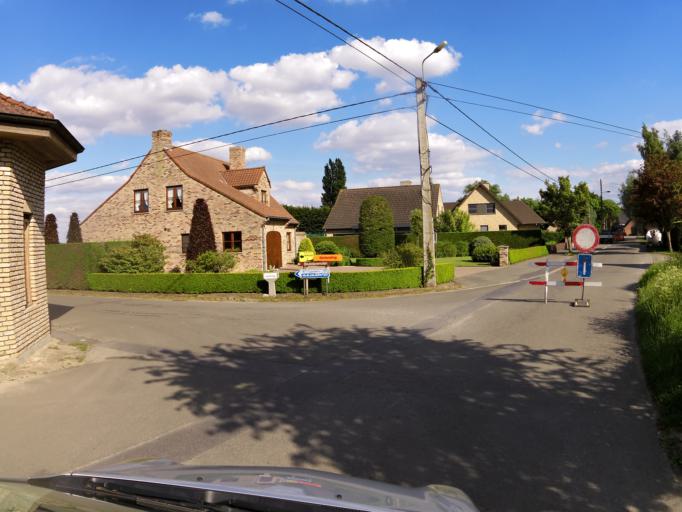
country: BE
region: Flanders
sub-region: Provincie West-Vlaanderen
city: Diksmuide
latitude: 50.9638
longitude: 2.8376
